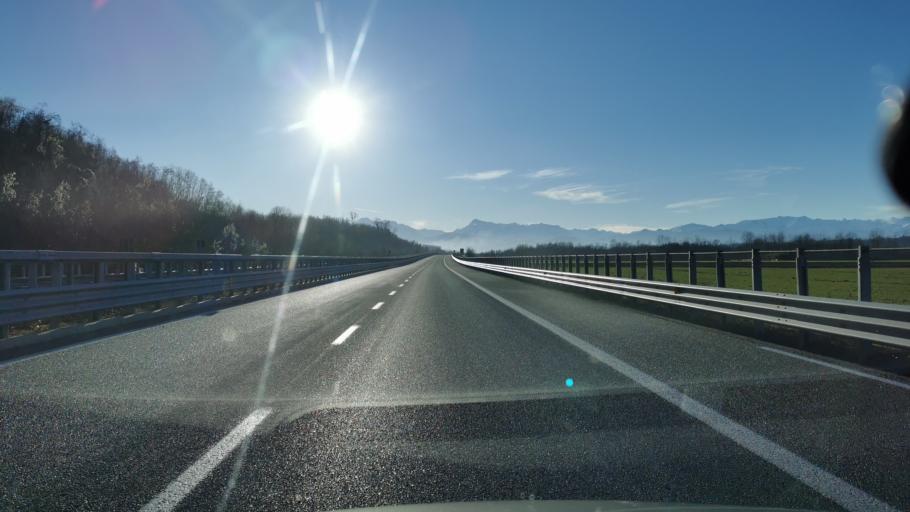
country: IT
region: Piedmont
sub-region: Provincia di Cuneo
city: Montanera
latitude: 44.4564
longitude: 7.6536
